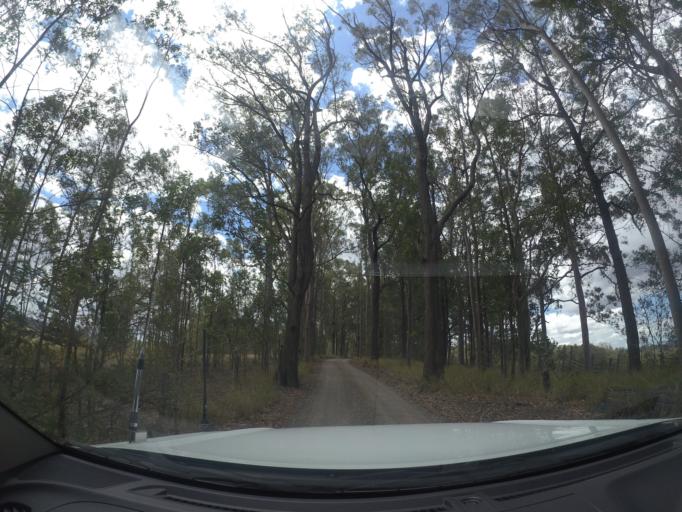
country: AU
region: Queensland
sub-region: Logan
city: Cedar Vale
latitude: -27.9112
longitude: 153.0313
